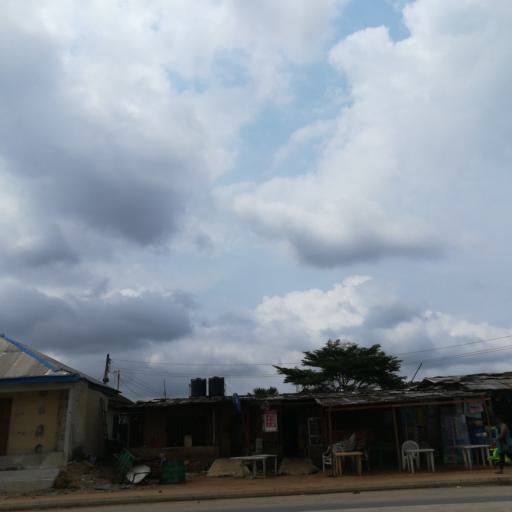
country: NG
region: Rivers
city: Port Harcourt
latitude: 4.8423
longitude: 7.0674
